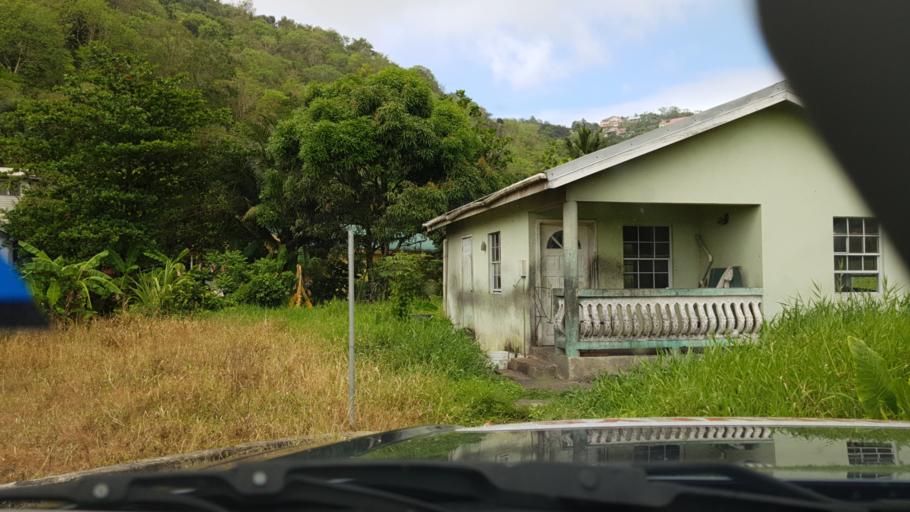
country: LC
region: Anse-la-Raye
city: Anse La Raye
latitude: 13.9420
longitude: -61.0404
